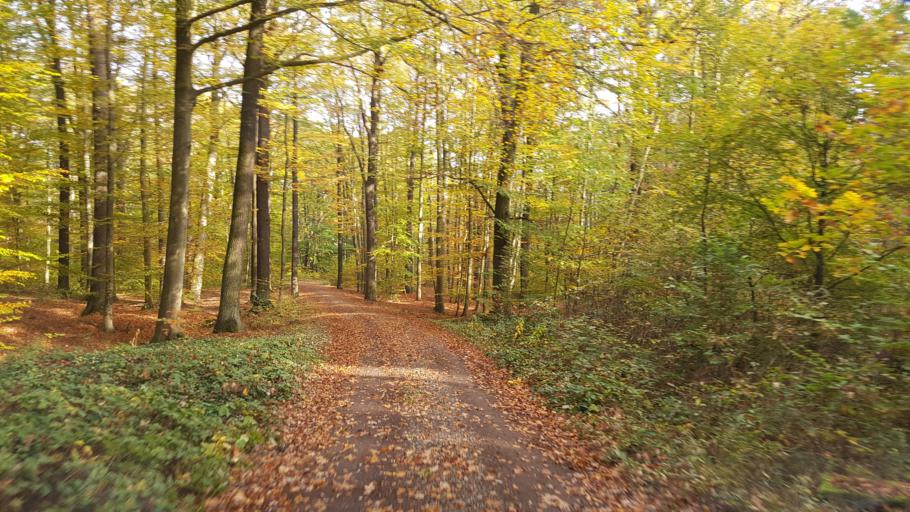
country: DE
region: Brandenburg
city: Doberlug-Kirchhain
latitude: 51.6281
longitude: 13.5256
